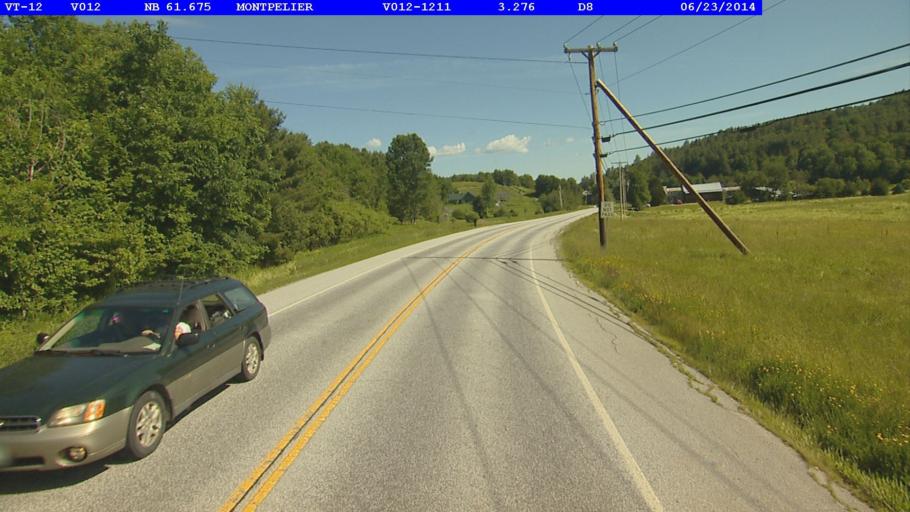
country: US
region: Vermont
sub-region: Washington County
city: Montpelier
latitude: 44.2890
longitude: -72.5792
